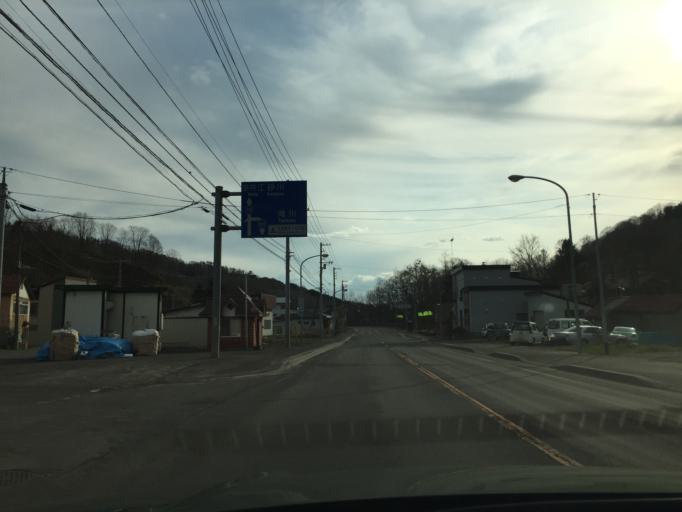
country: JP
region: Hokkaido
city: Utashinai
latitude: 43.5081
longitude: 142.0232
